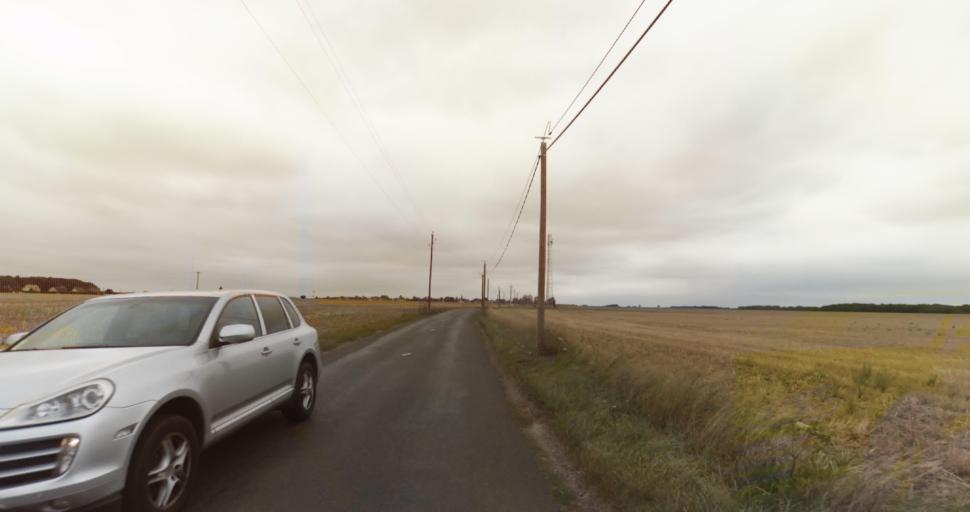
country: FR
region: Haute-Normandie
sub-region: Departement de l'Eure
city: La Couture-Boussey
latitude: 48.8988
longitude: 1.3582
